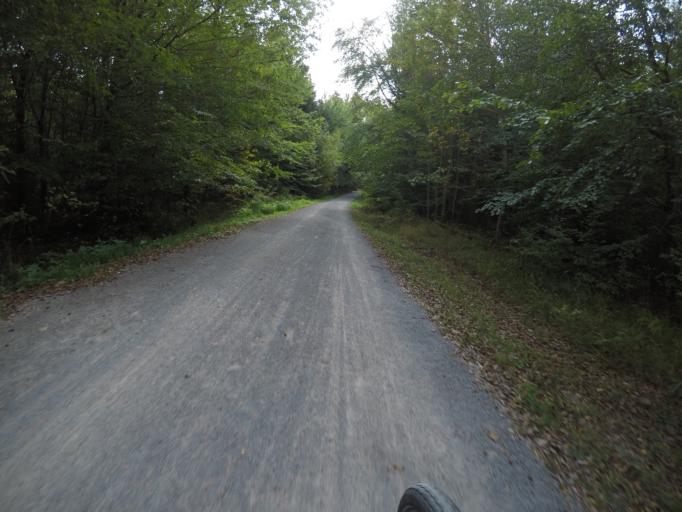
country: DE
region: Baden-Wuerttemberg
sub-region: Regierungsbezirk Stuttgart
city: Schonaich
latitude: 48.6743
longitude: 9.0507
